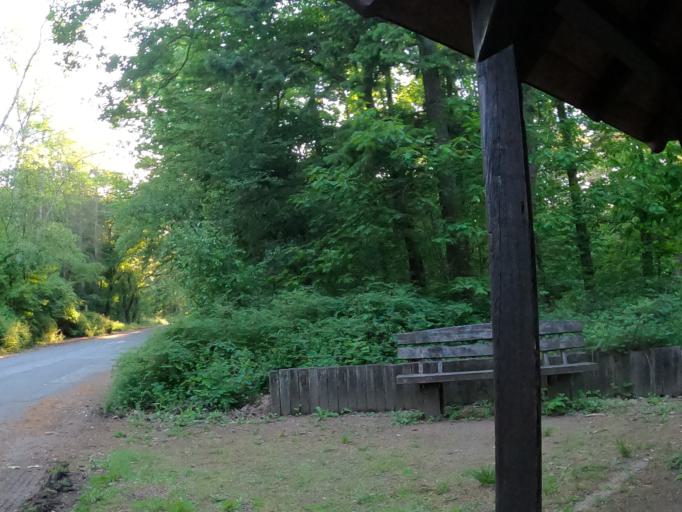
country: DE
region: Hesse
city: Kelsterbach
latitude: 50.0639
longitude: 8.5579
